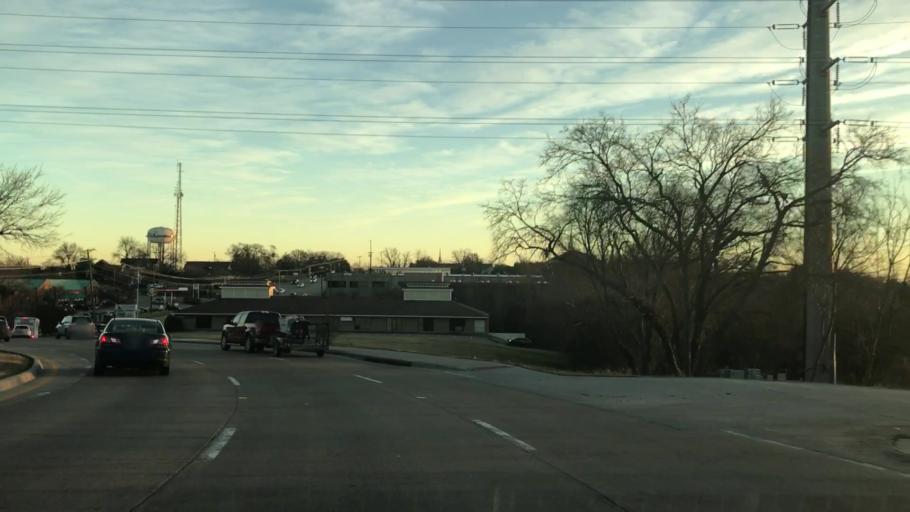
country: US
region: Texas
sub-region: Rockwall County
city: Rockwall
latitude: 32.9298
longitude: -96.4612
